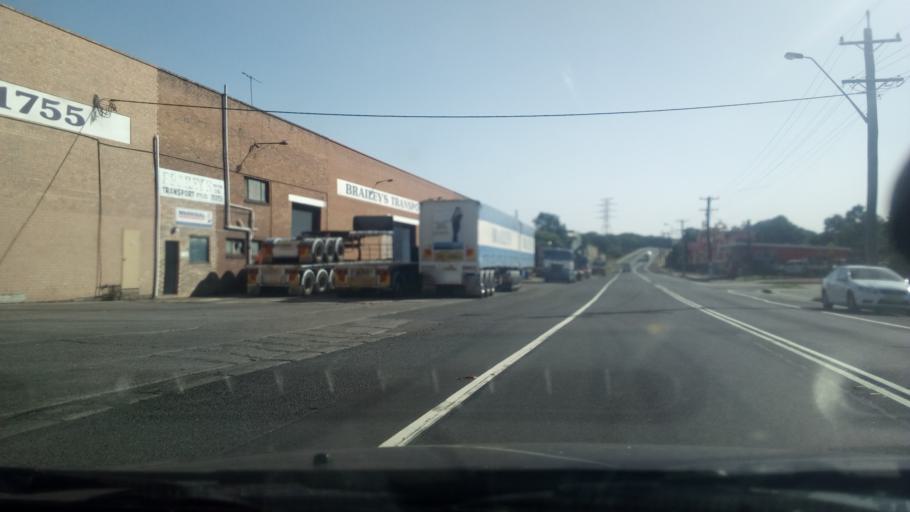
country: AU
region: New South Wales
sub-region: Wollongong
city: Cringila
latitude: -34.4703
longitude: 150.8933
